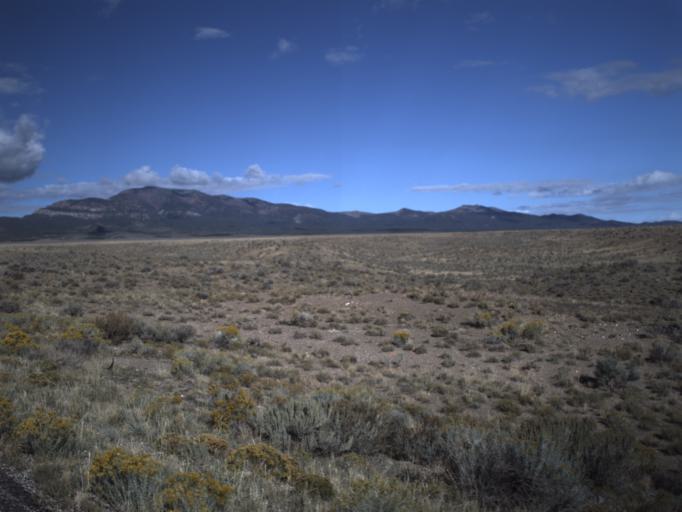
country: US
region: Utah
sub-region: Beaver County
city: Milford
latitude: 38.4402
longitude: -113.1597
